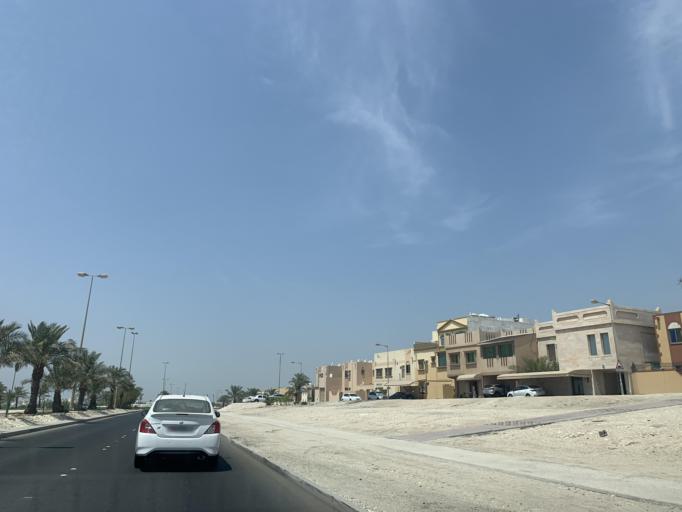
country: BH
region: Central Governorate
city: Madinat Hamad
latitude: 26.1216
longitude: 50.5023
